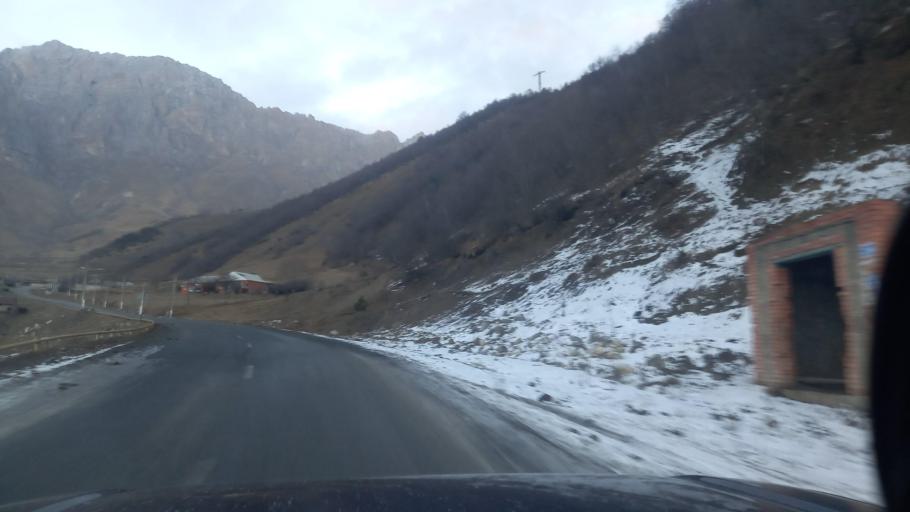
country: RU
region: Ingushetiya
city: Dzhayrakh
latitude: 42.8124
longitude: 44.8119
